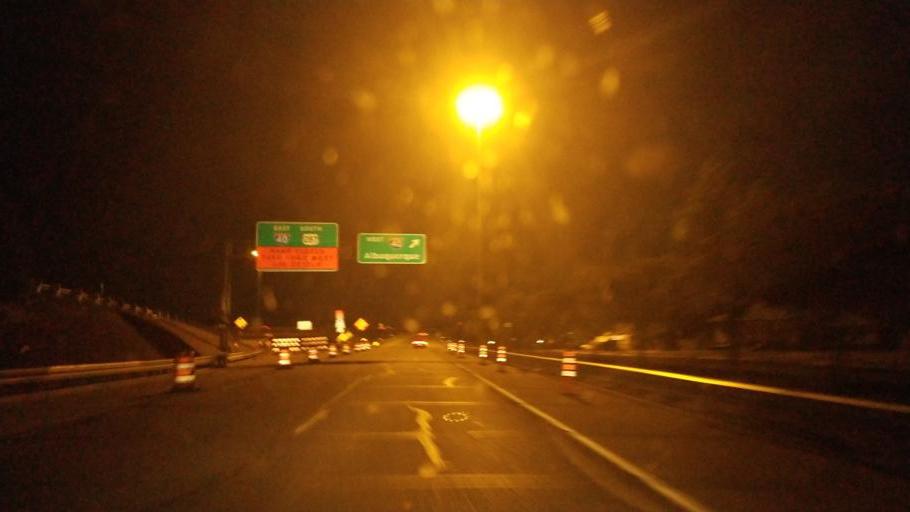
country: US
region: Texas
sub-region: Potter County
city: Amarillo
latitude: 35.1949
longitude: -101.8375
